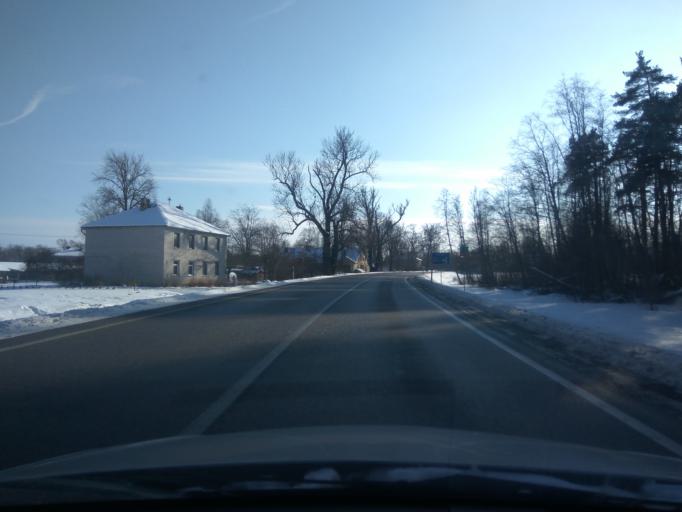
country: LV
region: Kuldigas Rajons
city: Kuldiga
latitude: 57.2831
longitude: 22.0235
